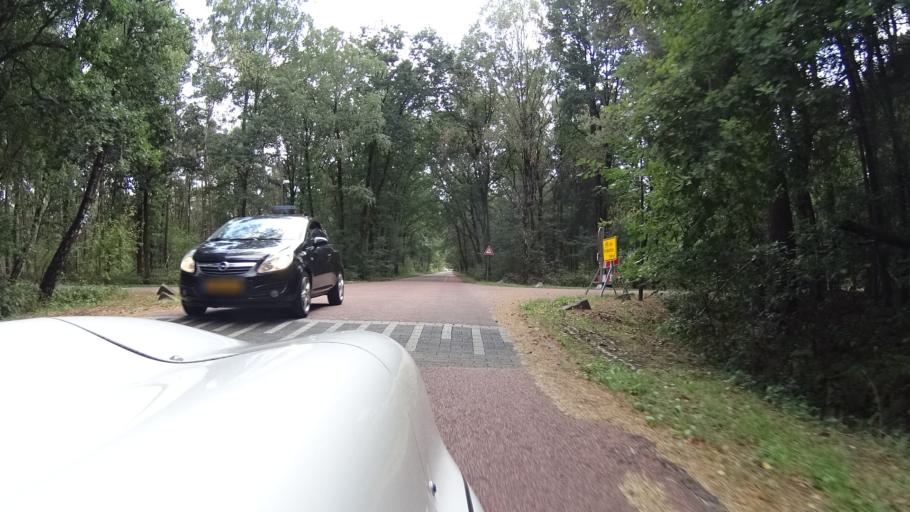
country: NL
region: North Brabant
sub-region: Gemeente Bernheze
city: Loosbroek
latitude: 51.6701
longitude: 5.4625
